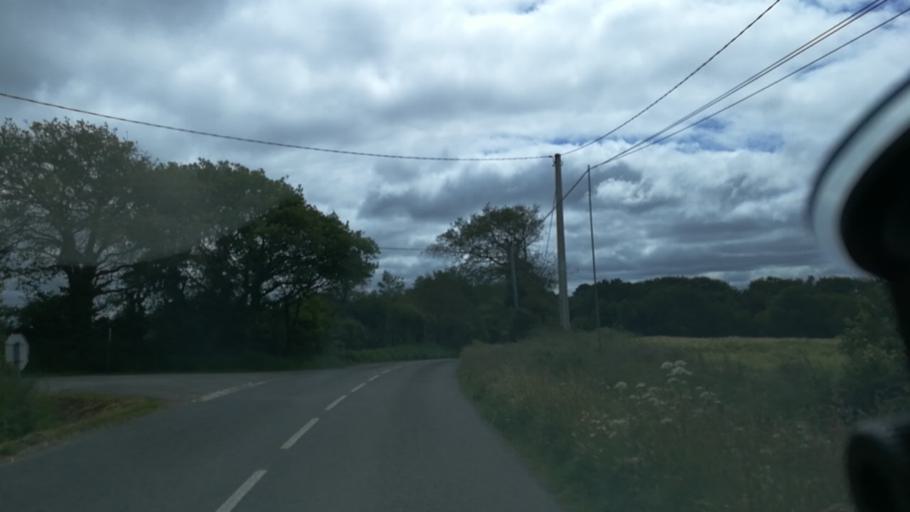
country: FR
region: Brittany
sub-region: Departement du Morbihan
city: Penestin
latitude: 47.4650
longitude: -2.4285
